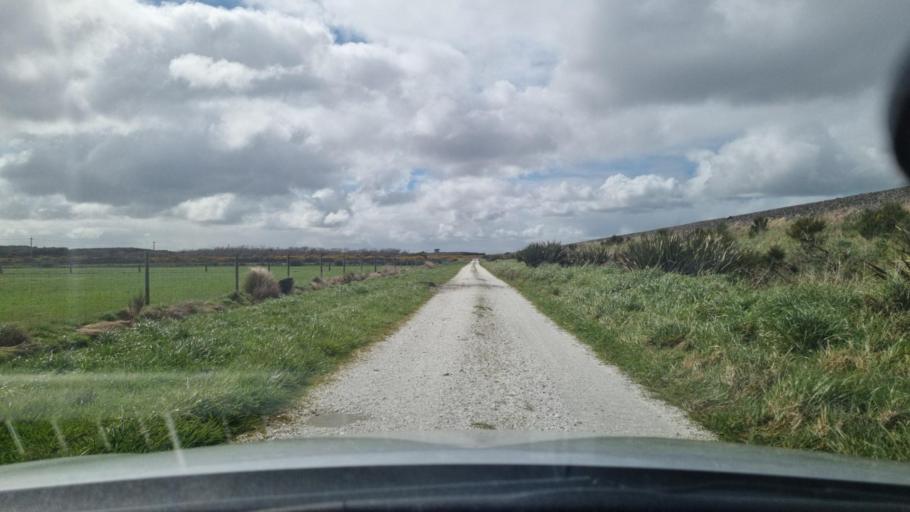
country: NZ
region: Southland
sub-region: Invercargill City
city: Bluff
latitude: -46.5342
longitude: 168.3043
